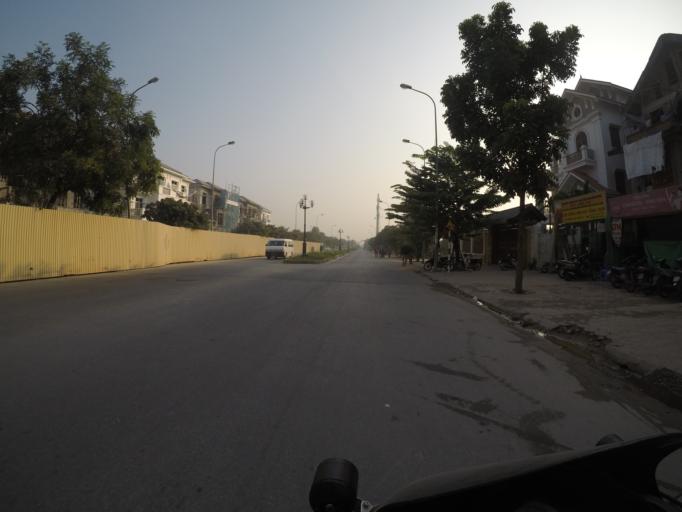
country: VN
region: Ha Noi
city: Trau Quy
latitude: 21.0415
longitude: 105.9105
